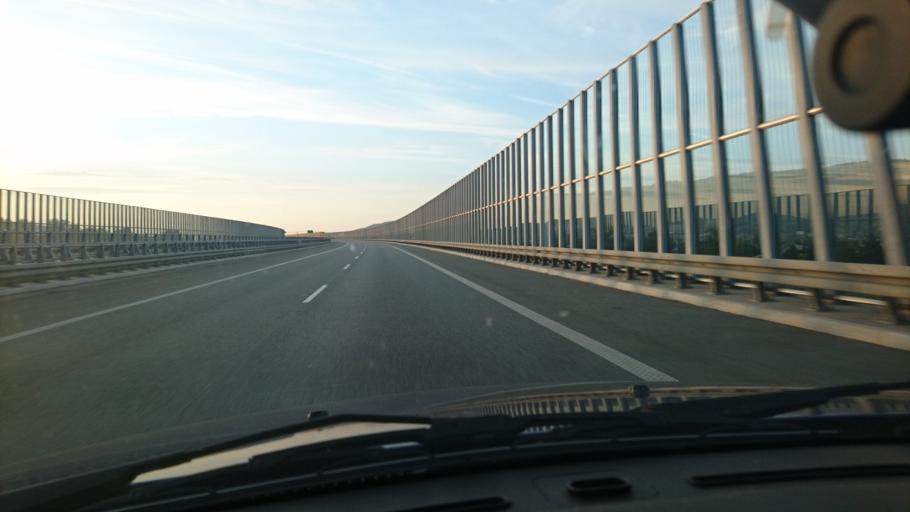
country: PL
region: Silesian Voivodeship
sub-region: Powiat bielski
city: Rybarzowice
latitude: 49.7318
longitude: 19.1163
